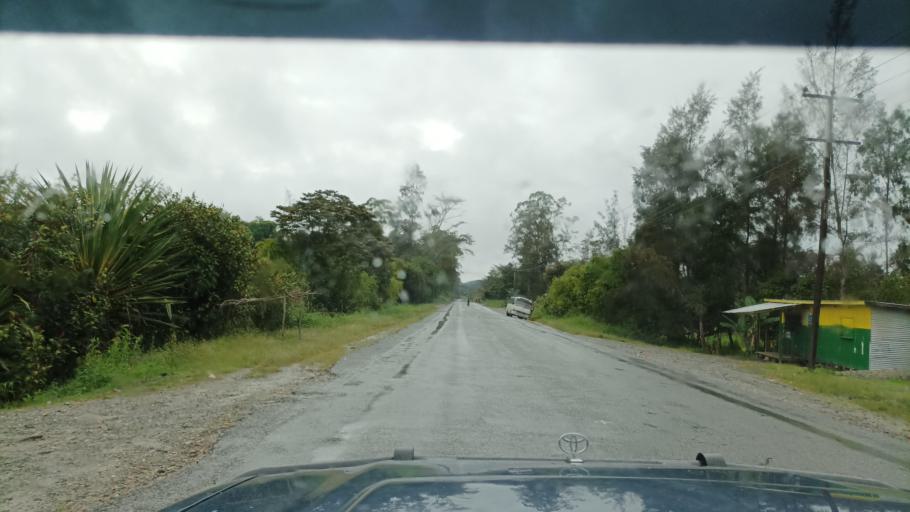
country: PG
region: Western Highlands
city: Rauna
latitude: -5.8231
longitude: 144.3981
